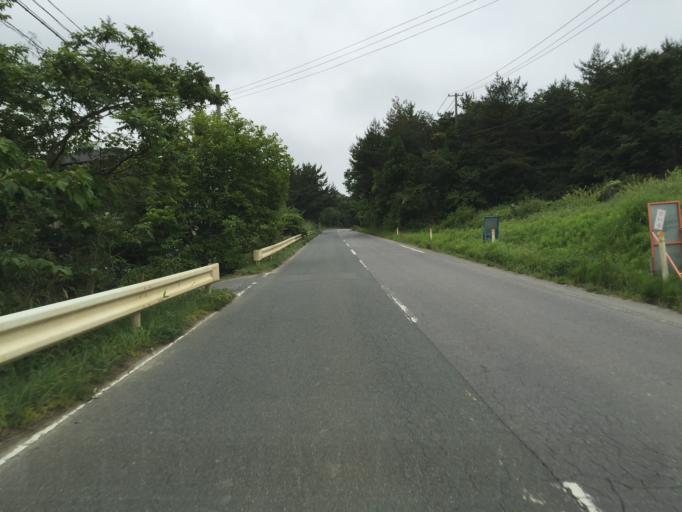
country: JP
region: Fukushima
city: Namie
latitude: 37.7373
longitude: 141.0052
